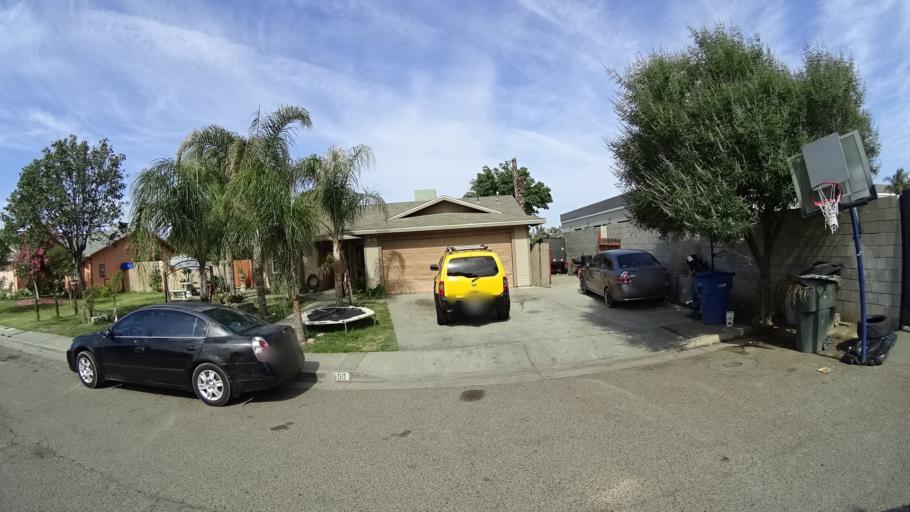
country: US
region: California
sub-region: Kings County
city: Hanford
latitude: 36.3189
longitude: -119.6603
